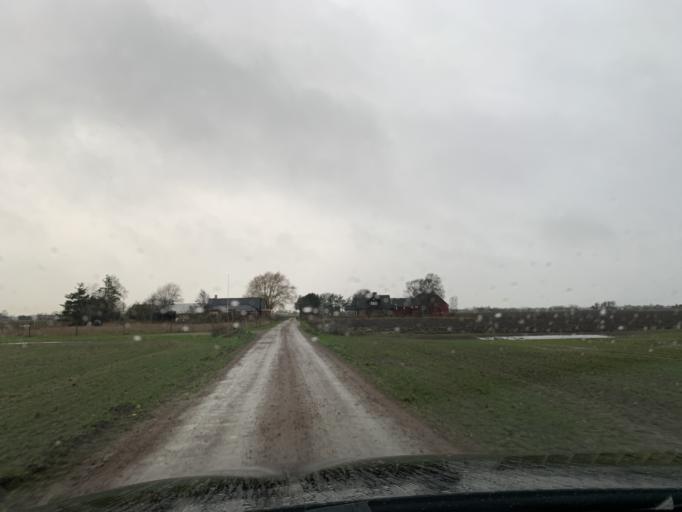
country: SE
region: Skane
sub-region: Kavlinge Kommun
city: Hofterup
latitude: 55.8458
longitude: 12.9925
